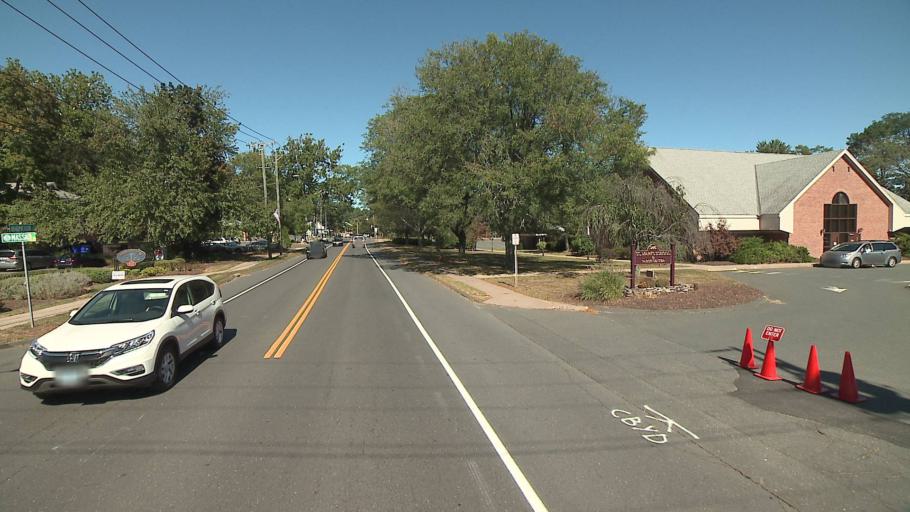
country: US
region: Connecticut
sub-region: Hartford County
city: Simsbury Center
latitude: 41.8813
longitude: -72.7998
